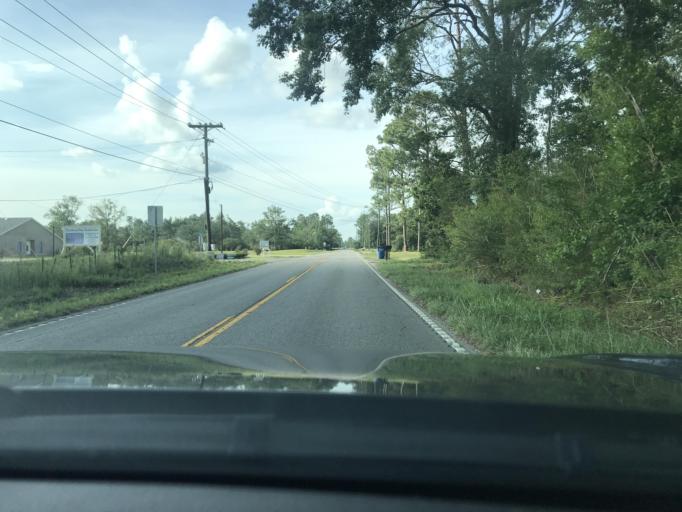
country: US
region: Louisiana
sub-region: Calcasieu Parish
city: Moss Bluff
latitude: 30.3220
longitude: -93.2582
